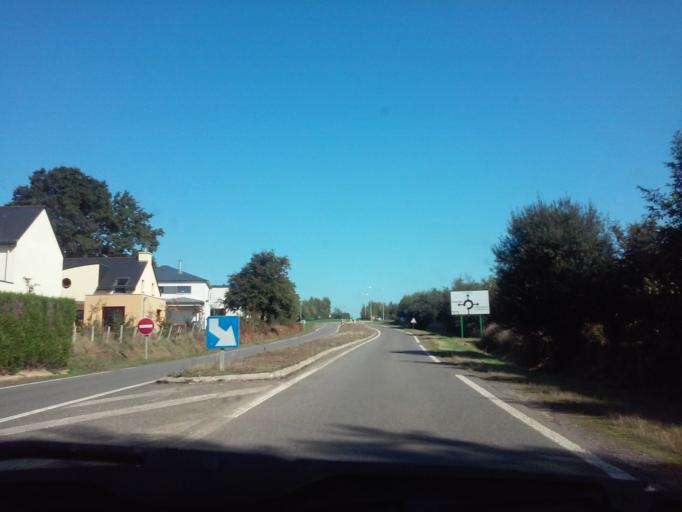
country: FR
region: Brittany
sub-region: Departement d'Ille-et-Vilaine
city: Chevaigne
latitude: 48.2076
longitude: -1.6255
